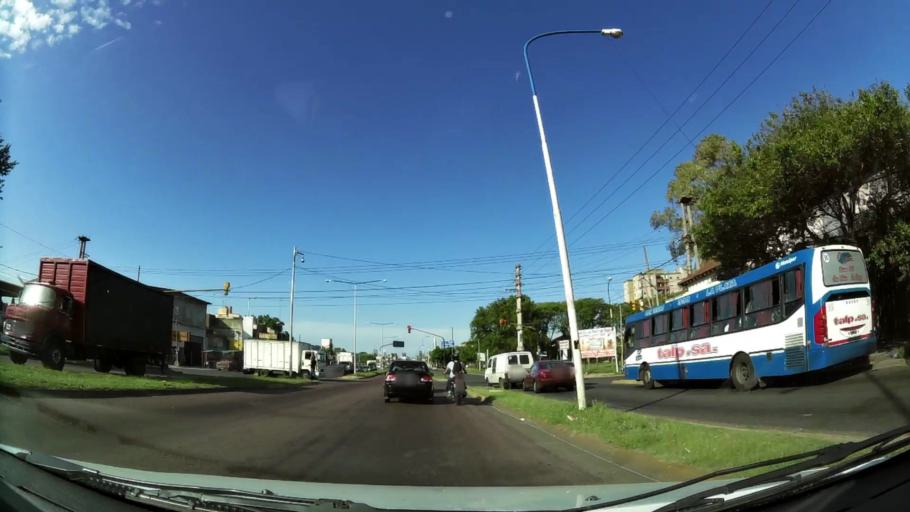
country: AR
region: Buenos Aires
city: Hurlingham
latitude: -34.5816
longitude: -58.6018
